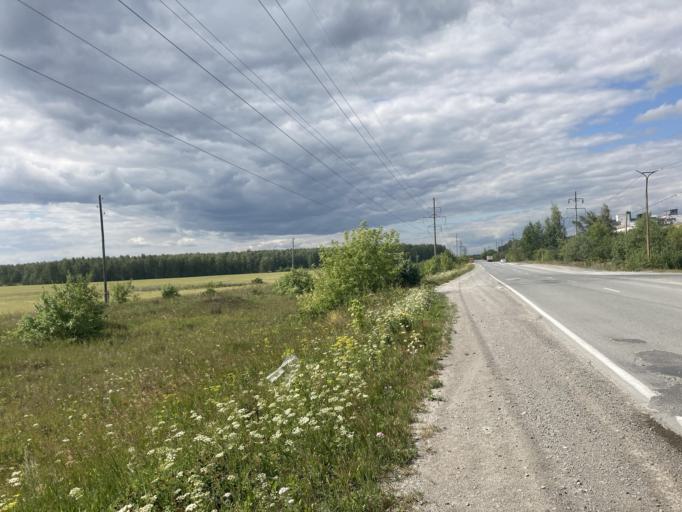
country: RU
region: Sverdlovsk
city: Bogdanovich
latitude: 56.8022
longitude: 62.0370
